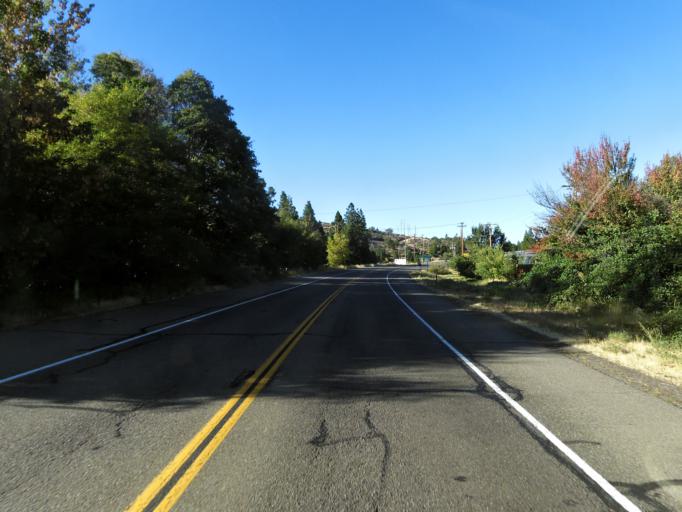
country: US
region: California
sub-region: Siskiyou County
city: Weed
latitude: 41.4282
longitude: -122.3893
